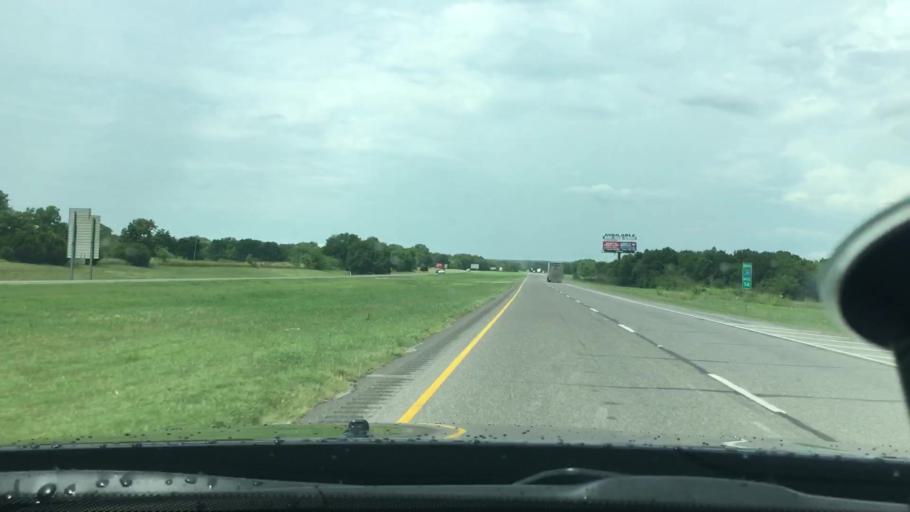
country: US
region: Oklahoma
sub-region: Murray County
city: Davis
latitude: 34.5105
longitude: -97.1768
